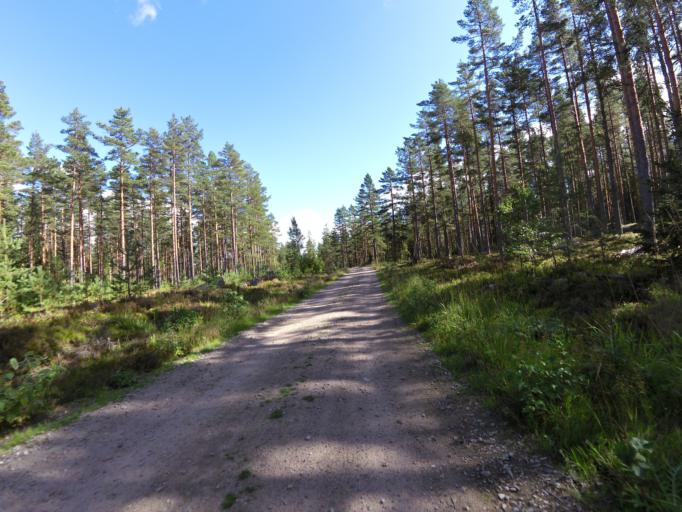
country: SE
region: Gaevleborg
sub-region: Ockelbo Kommun
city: Ockelbo
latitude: 60.8395
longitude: 16.7654
